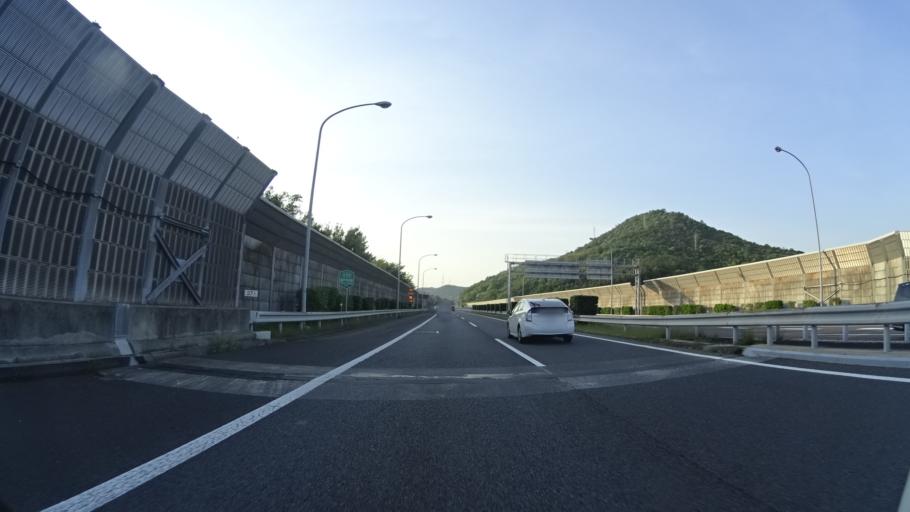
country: JP
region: Kagawa
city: Sakaidecho
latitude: 34.2990
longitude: 133.8432
